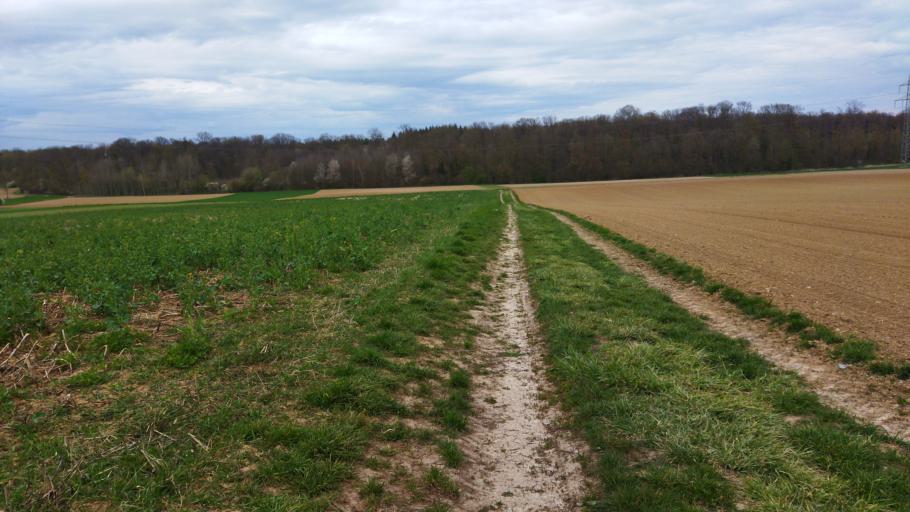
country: DE
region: Baden-Wuerttemberg
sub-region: Regierungsbezirk Stuttgart
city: Oedheim
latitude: 49.2218
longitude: 9.2827
